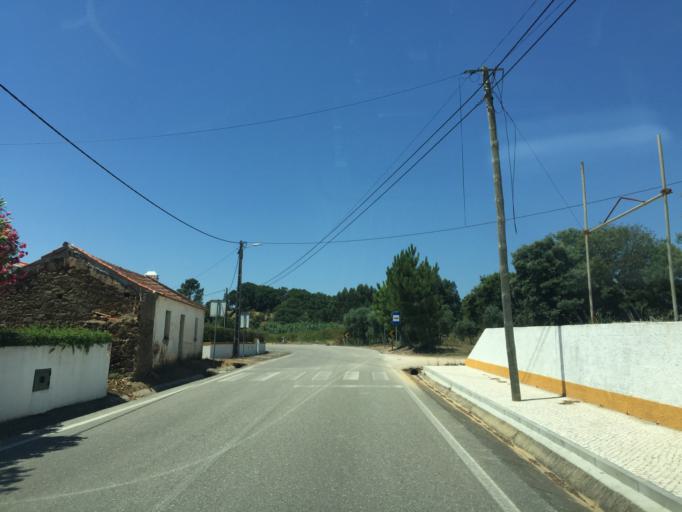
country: PT
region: Santarem
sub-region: Ferreira do Zezere
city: Ferreira do Zezere
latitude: 39.5949
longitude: -8.2749
